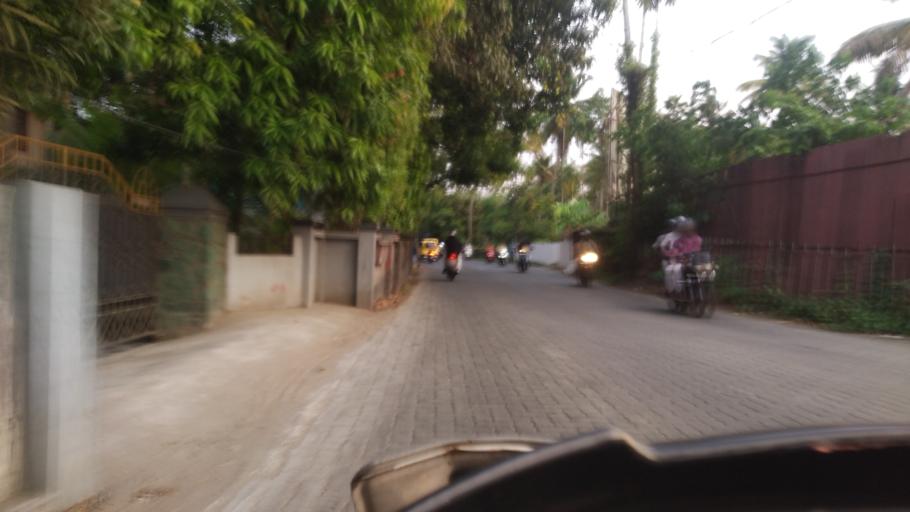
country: IN
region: Kerala
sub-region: Thrissur District
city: Kodungallur
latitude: 10.1817
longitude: 76.2049
